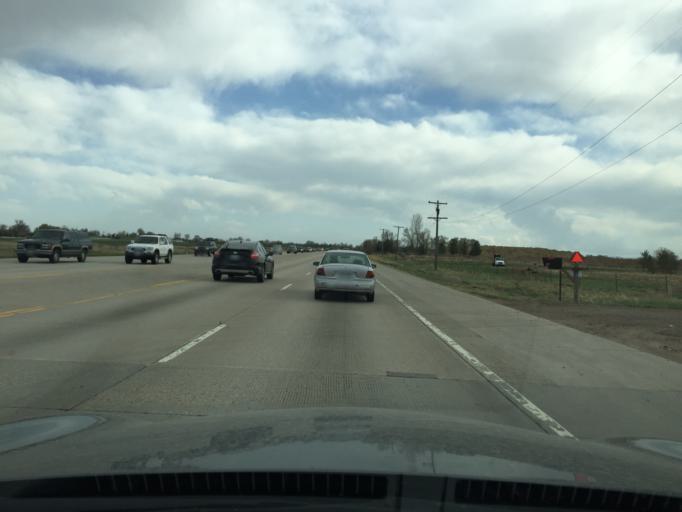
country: US
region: Colorado
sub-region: Boulder County
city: Erie
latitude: 40.0500
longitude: -105.1028
